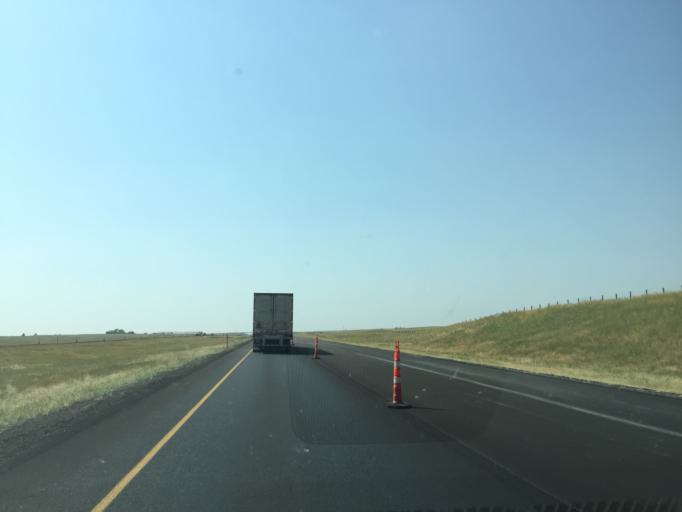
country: US
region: Wyoming
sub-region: Laramie County
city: Ranchettes
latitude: 41.3056
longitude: -104.8560
